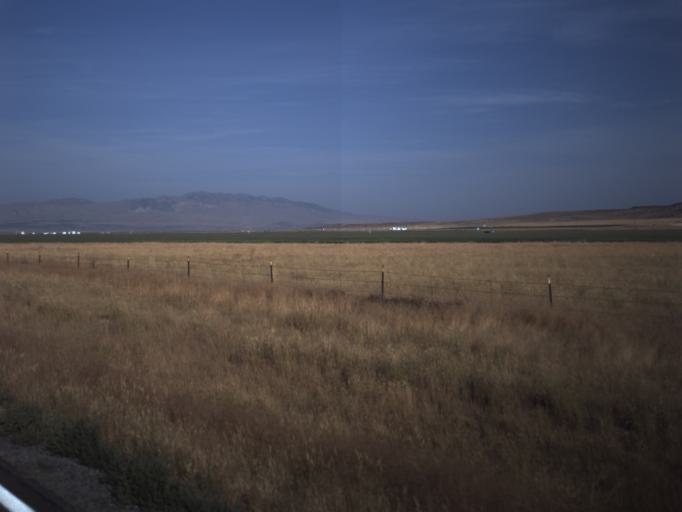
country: US
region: Idaho
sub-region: Oneida County
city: Malad City
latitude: 41.9664
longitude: -112.7773
